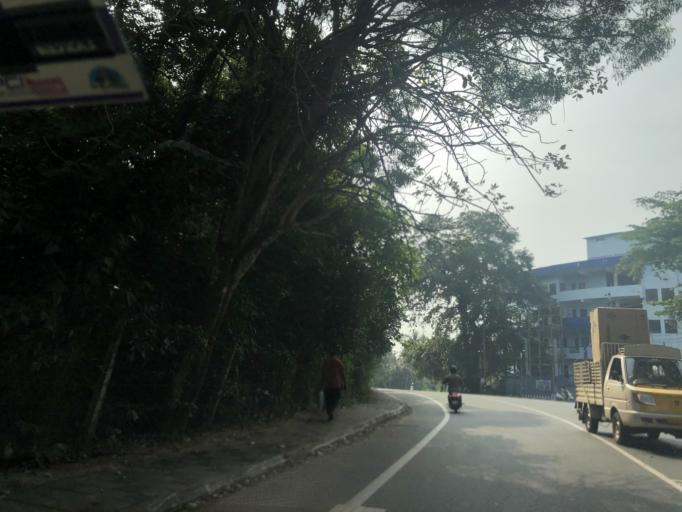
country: IN
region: Kerala
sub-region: Kozhikode
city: Kozhikode
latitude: 11.2918
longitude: 75.7690
